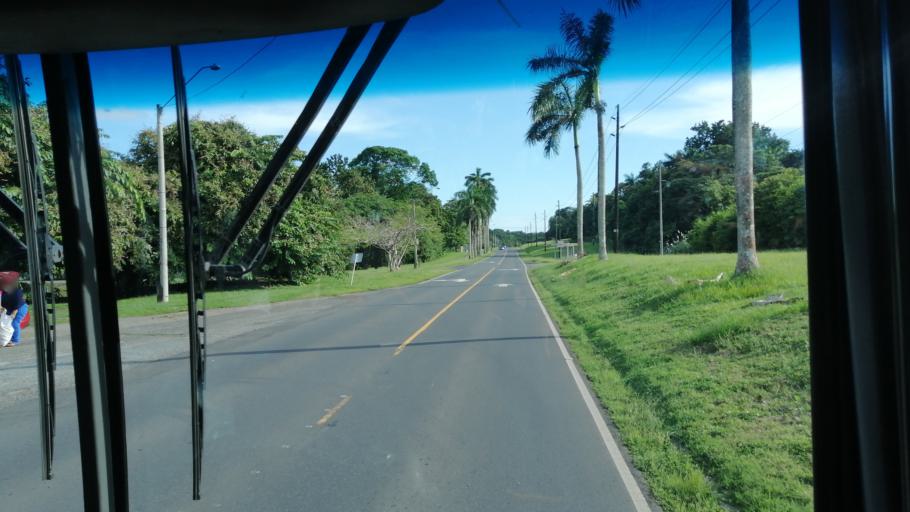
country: PA
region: Panama
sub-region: Distrito de Panama
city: Ancon
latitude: 8.9411
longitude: -79.5910
